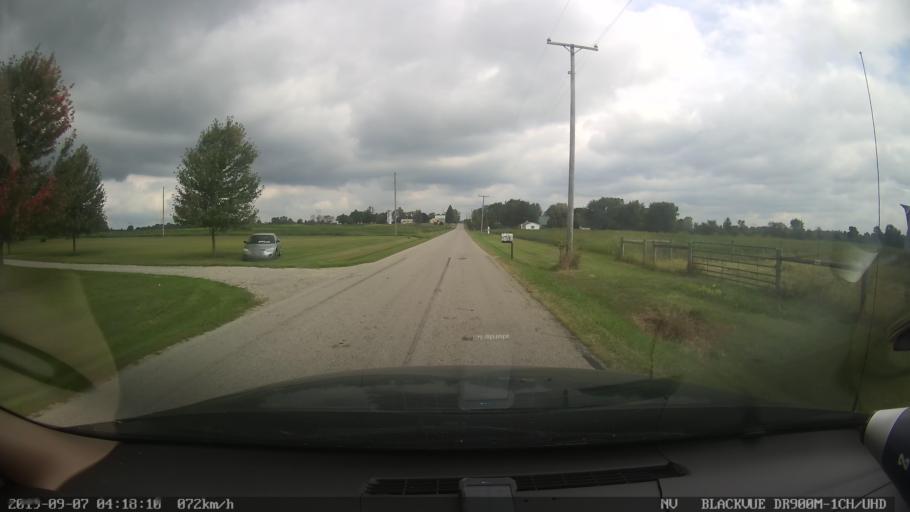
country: US
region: Ohio
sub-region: Knox County
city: Centerburg
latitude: 40.2522
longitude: -82.6635
